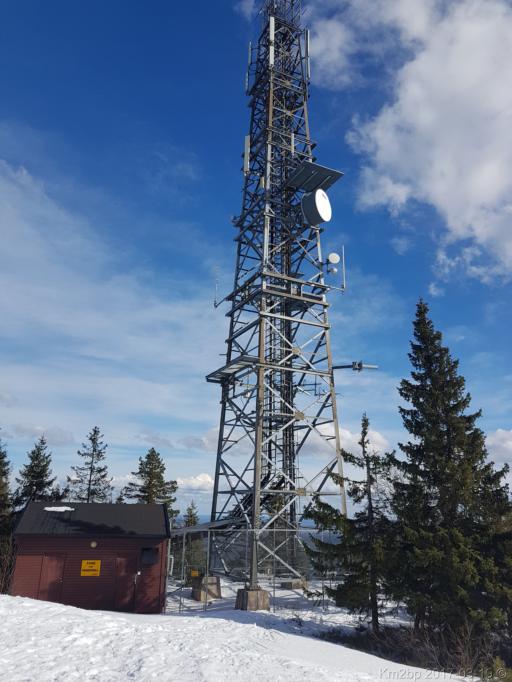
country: NO
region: Akershus
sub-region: Nittedal
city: Aneby
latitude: 60.0931
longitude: 10.8364
